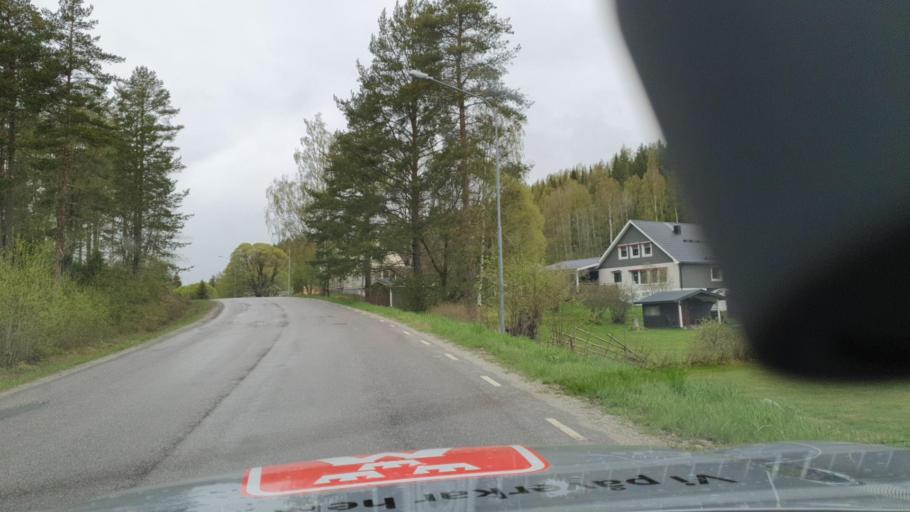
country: SE
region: Vaesternorrland
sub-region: OErnskoeldsviks Kommun
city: Ornskoldsvik
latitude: 63.3009
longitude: 18.5965
